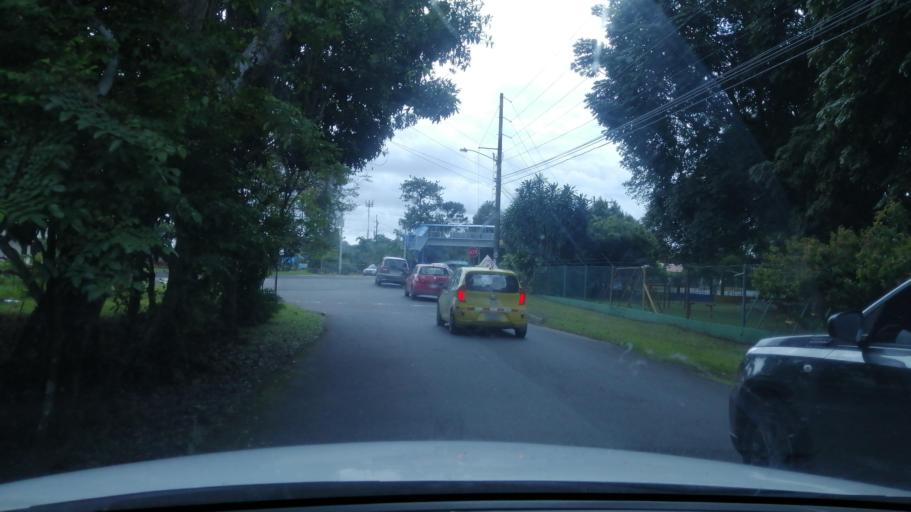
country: PA
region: Chiriqui
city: David
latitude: 8.4462
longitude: -82.4291
